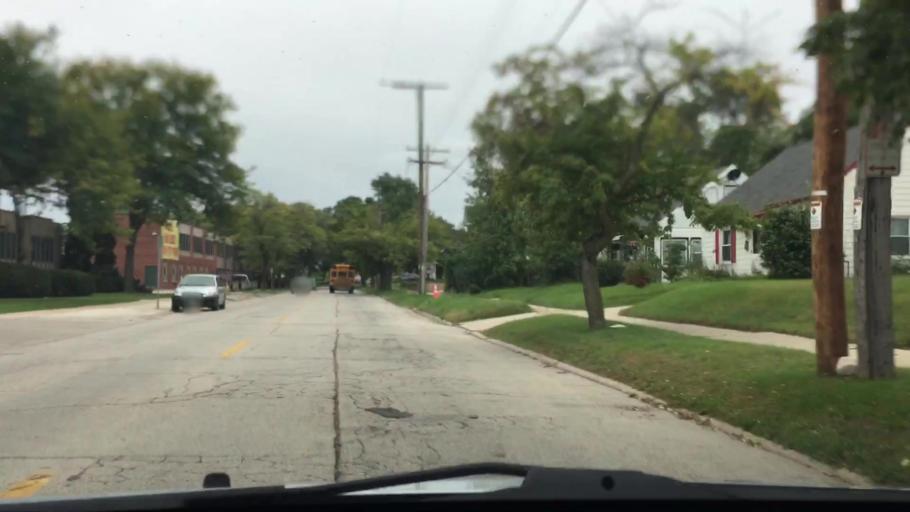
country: US
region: Wisconsin
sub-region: Waukesha County
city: Waukesha
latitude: 43.0175
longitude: -88.2135
